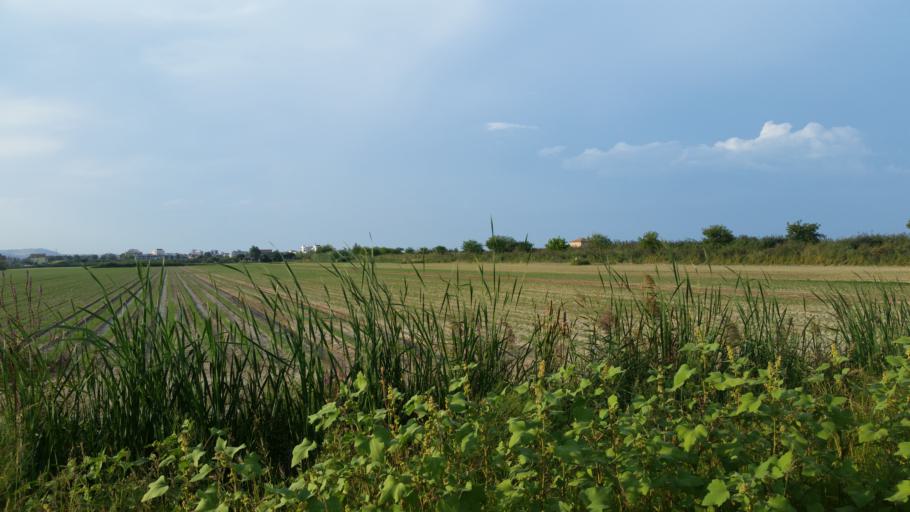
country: IT
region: Abruzzo
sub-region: Provincia di Teramo
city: Martinsicuro
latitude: 42.8992
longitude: 13.9080
